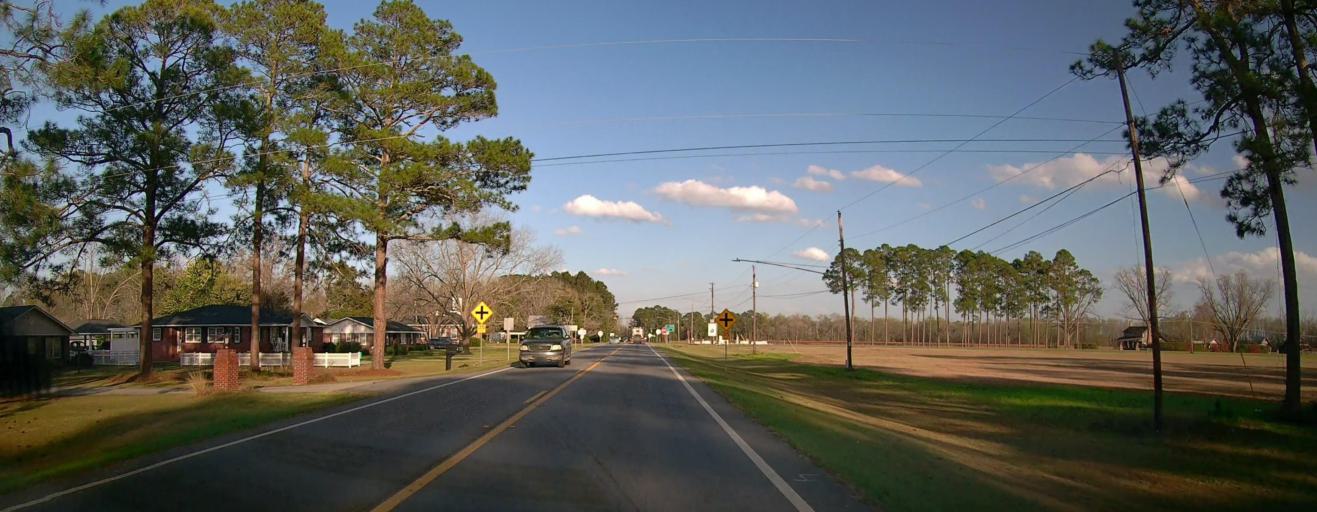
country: US
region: Georgia
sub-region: Evans County
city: Claxton
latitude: 32.1497
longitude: -81.9763
